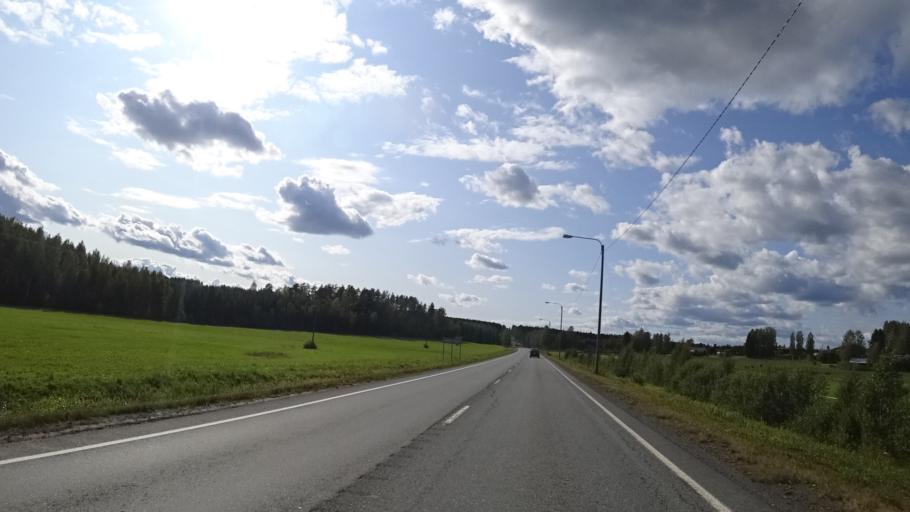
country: FI
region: North Karelia
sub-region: Keski-Karjala
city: Tohmajaervi
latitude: 62.2211
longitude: 30.3898
